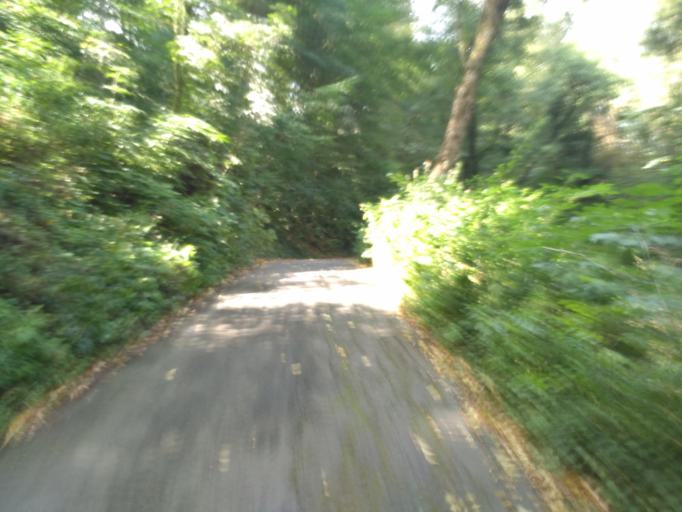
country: SK
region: Banskobystricky
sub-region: Okres Banska Bystrica
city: Banska Bystrica
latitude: 48.7313
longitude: 19.1804
